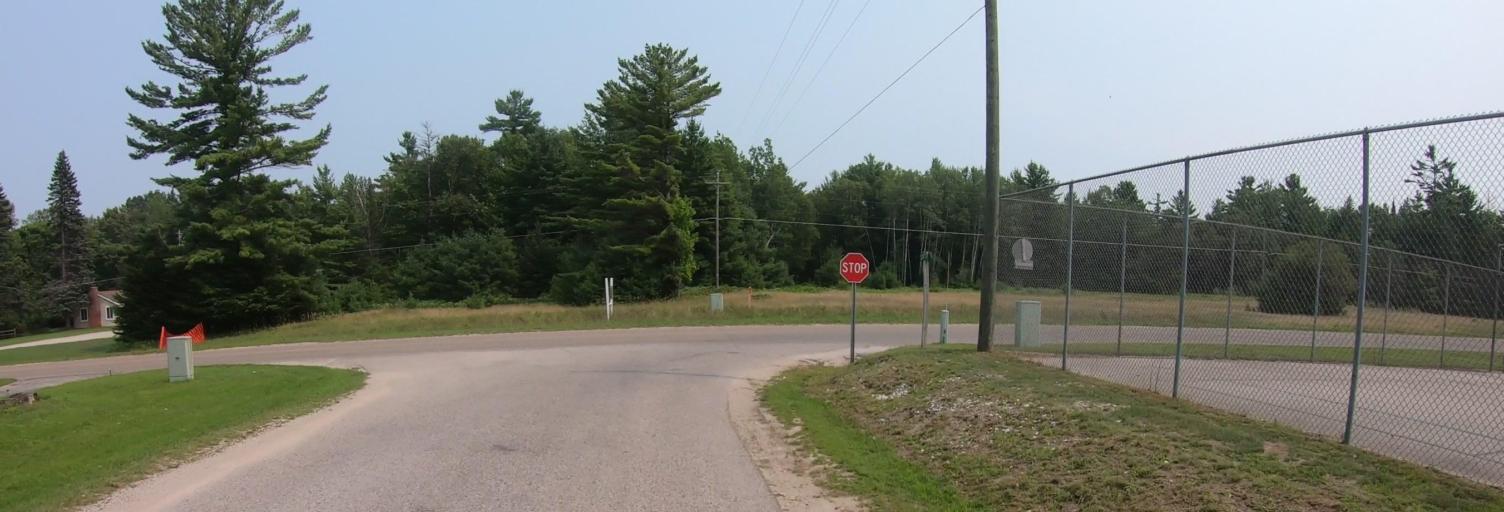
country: CA
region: Ontario
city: Thessalon
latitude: 46.0164
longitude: -83.7386
